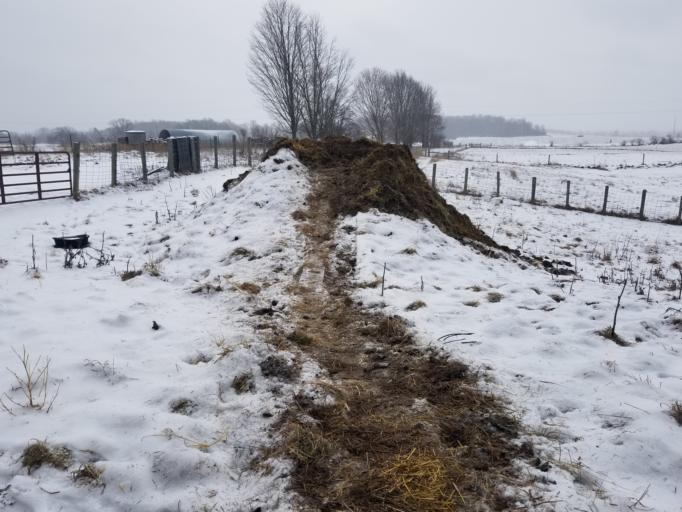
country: US
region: Michigan
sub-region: Mecosta County
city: Big Rapids
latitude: 43.7433
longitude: -85.4999
